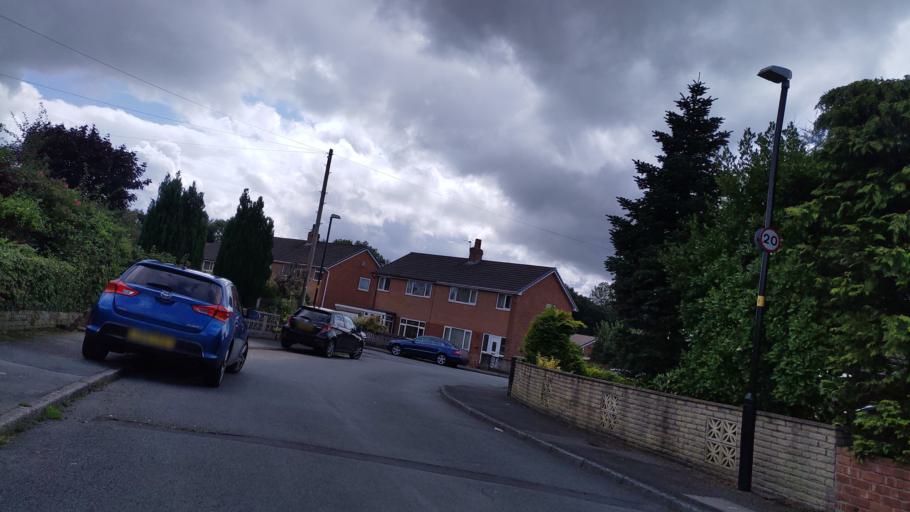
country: GB
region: England
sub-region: Lancashire
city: Coppull
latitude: 53.6498
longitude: -2.6465
